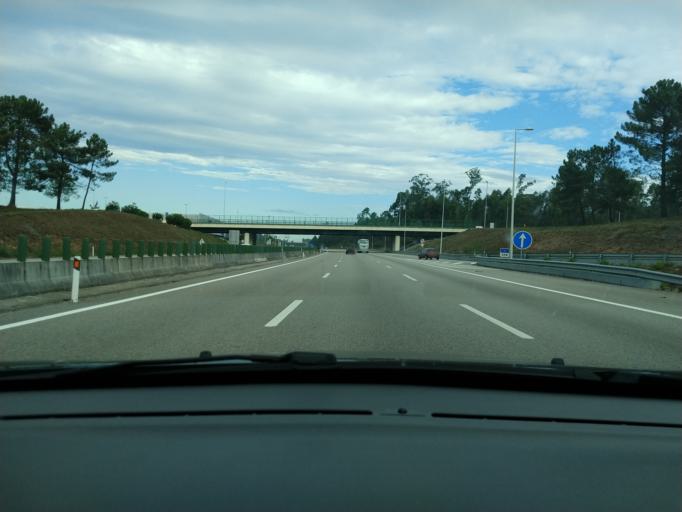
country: PT
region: Aveiro
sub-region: Estarreja
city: Beduido
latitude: 40.7808
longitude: -8.5442
